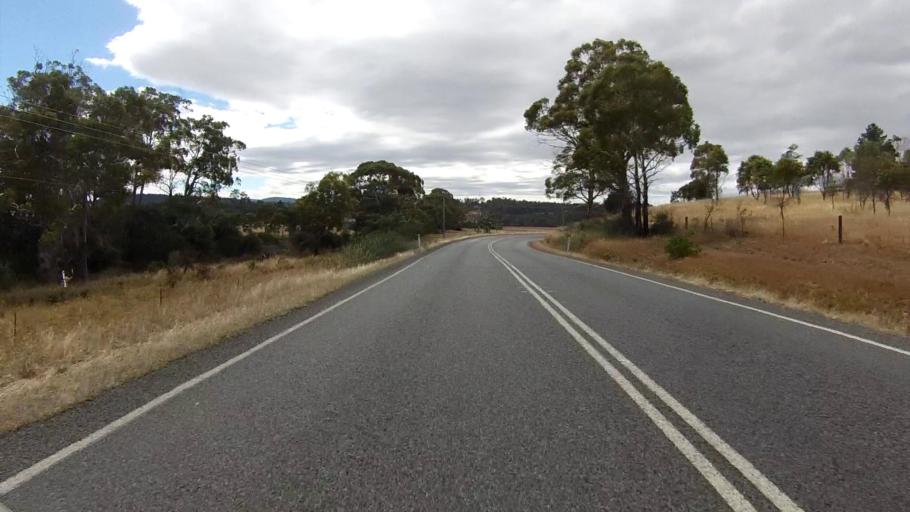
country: AU
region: Tasmania
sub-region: Sorell
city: Sorell
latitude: -42.6078
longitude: 147.6953
